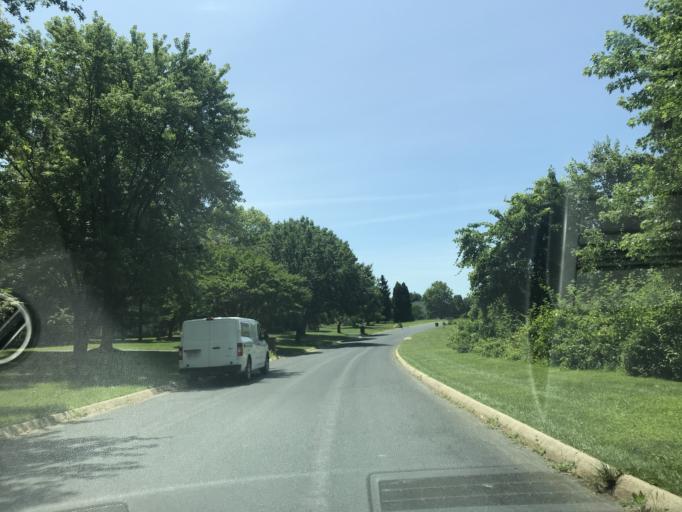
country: US
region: Maryland
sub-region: Harford County
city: South Bel Air
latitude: 39.5544
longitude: -76.2750
